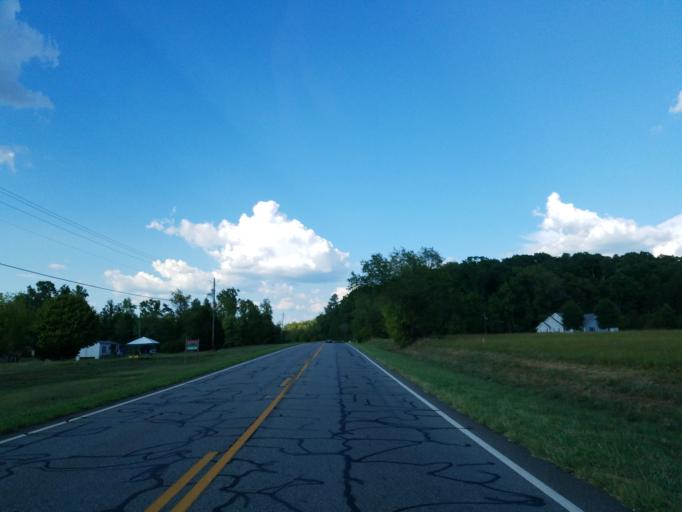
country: US
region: Georgia
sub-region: Bartow County
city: Rydal
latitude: 34.5204
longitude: -84.7081
